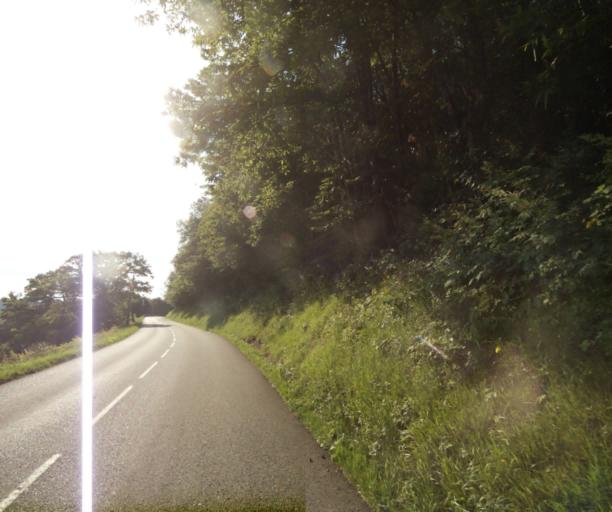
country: FR
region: Rhone-Alpes
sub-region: Departement de la Haute-Savoie
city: Armoy
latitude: 46.3598
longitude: 6.5134
